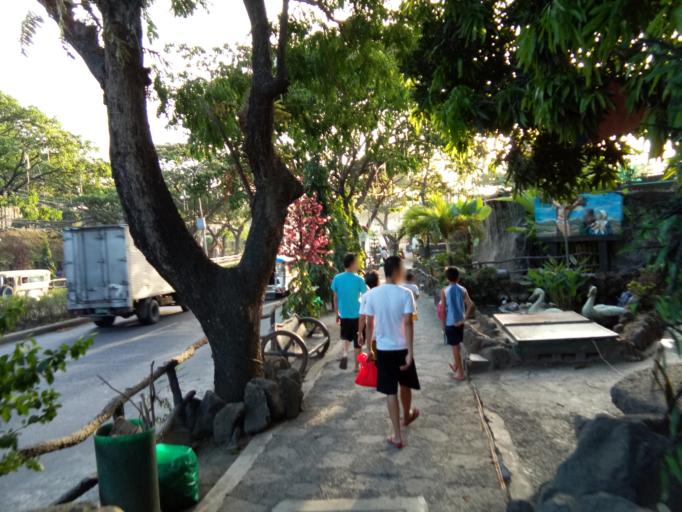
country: PH
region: Calabarzon
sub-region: Province of Cavite
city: Dasmarinas
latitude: 14.3287
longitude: 120.9576
